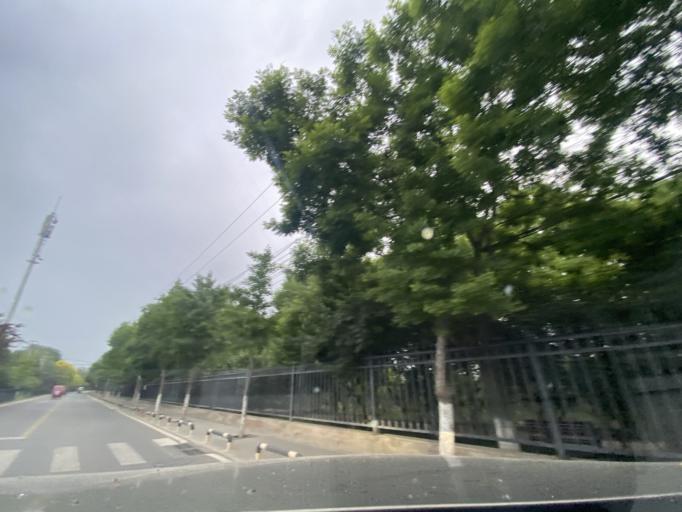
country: CN
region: Beijing
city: Sijiqing
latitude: 39.9546
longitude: 116.2501
